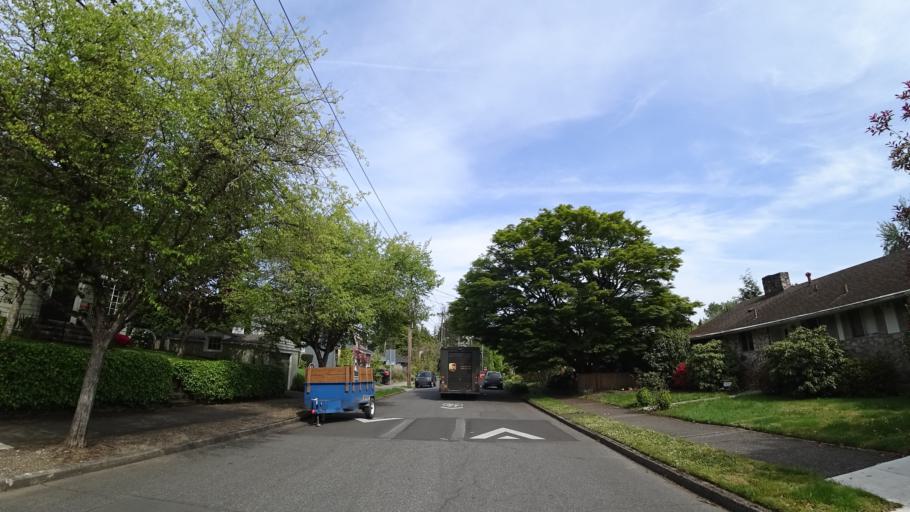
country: US
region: Oregon
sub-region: Clackamas County
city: Milwaukie
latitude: 45.4650
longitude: -122.6173
